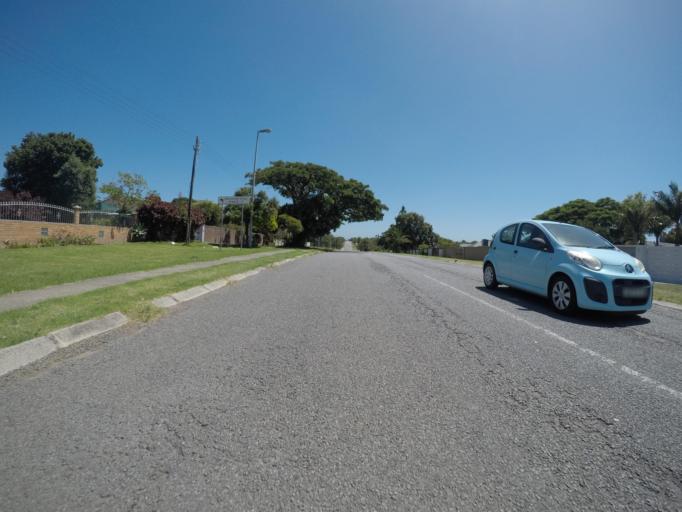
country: ZA
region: Eastern Cape
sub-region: Buffalo City Metropolitan Municipality
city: East London
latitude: -32.9727
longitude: 27.9412
